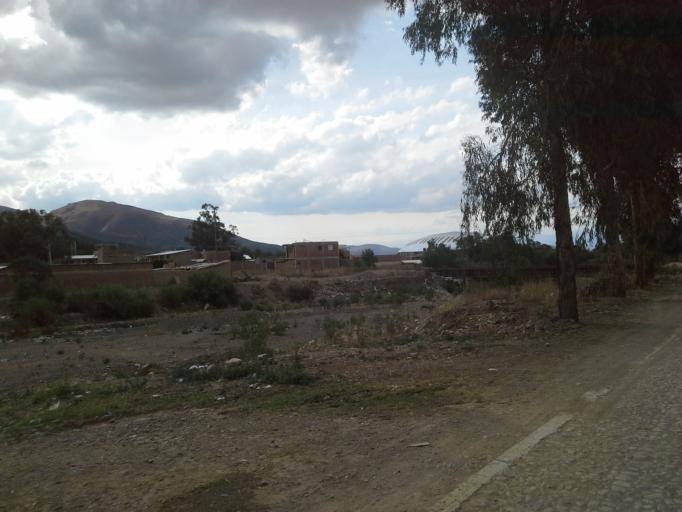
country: BO
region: Cochabamba
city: Tarata
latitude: -17.6087
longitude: -66.0210
